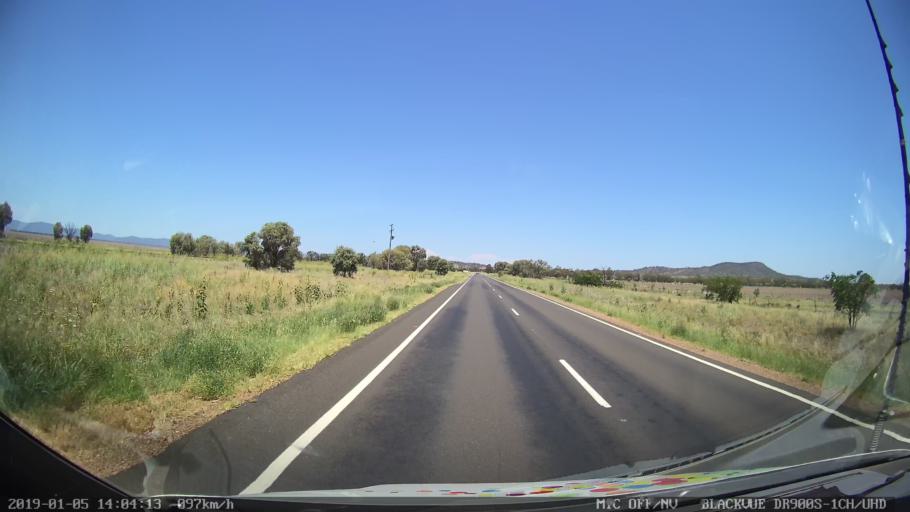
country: AU
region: New South Wales
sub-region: Gunnedah
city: Gunnedah
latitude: -31.1977
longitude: 150.3610
